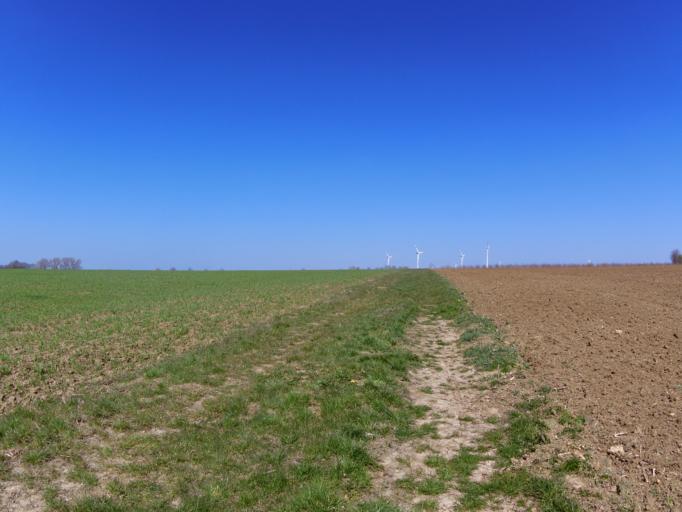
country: DE
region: Bavaria
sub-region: Regierungsbezirk Unterfranken
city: Biebelried
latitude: 49.7368
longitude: 10.0979
